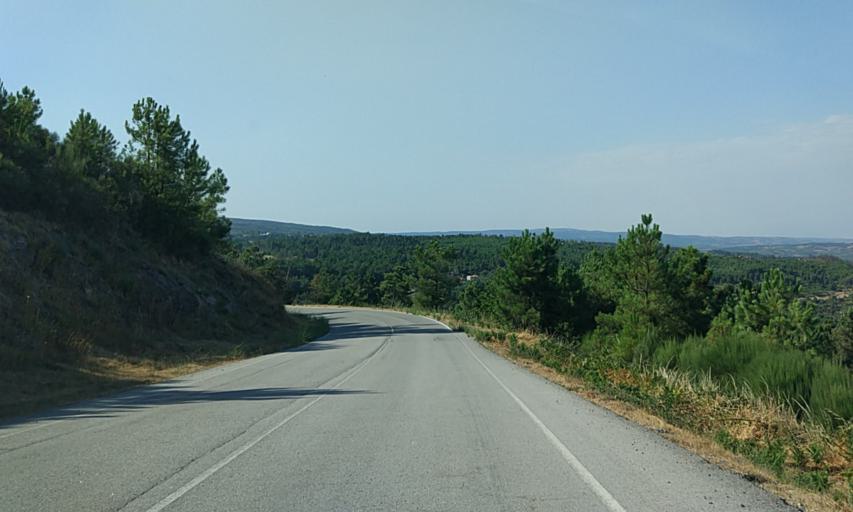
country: PT
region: Vila Real
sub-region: Murca
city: Murca
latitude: 41.3567
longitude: -7.4818
